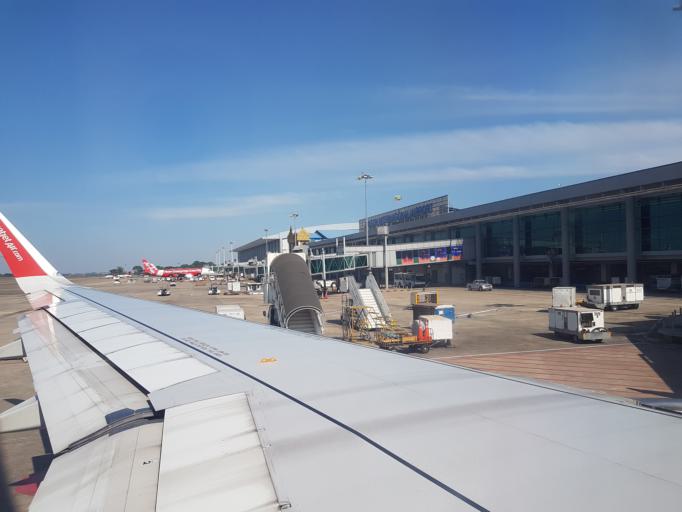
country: MM
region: Yangon
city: Yangon
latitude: 16.9003
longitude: 96.1325
